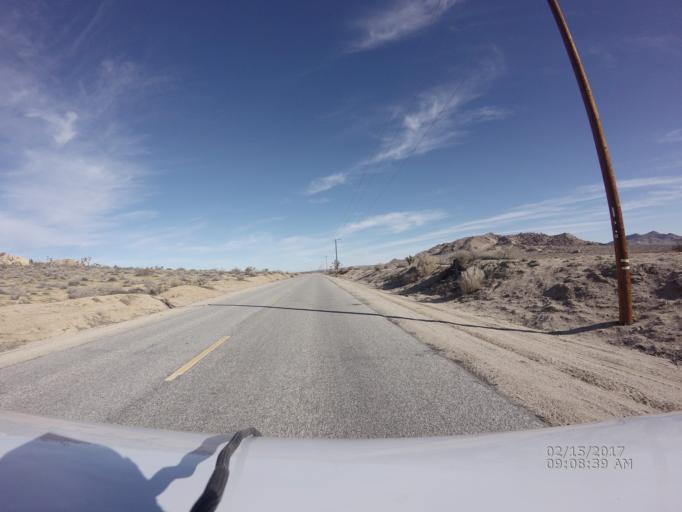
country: US
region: California
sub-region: Los Angeles County
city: Lake Los Angeles
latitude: 34.6422
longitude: -117.8629
